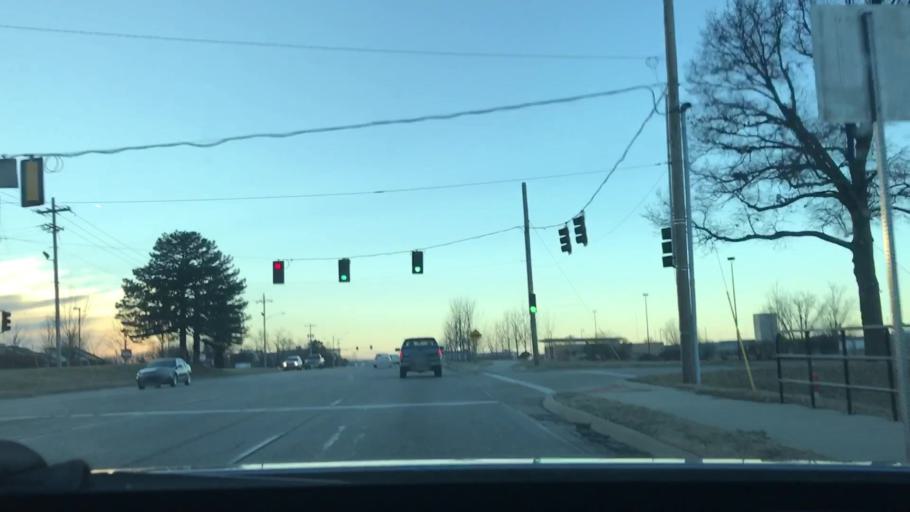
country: US
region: Kansas
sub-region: Wyandotte County
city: Edwardsville
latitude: 39.1165
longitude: -94.7990
